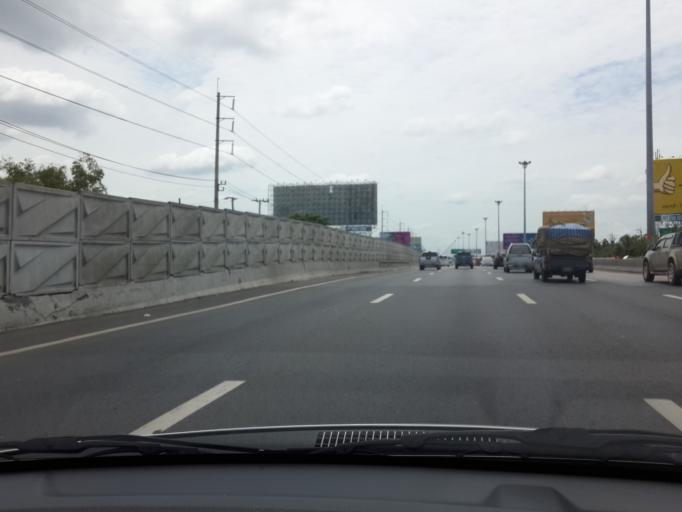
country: TH
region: Bangkok
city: Suan Luang
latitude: 13.7359
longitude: 100.6739
